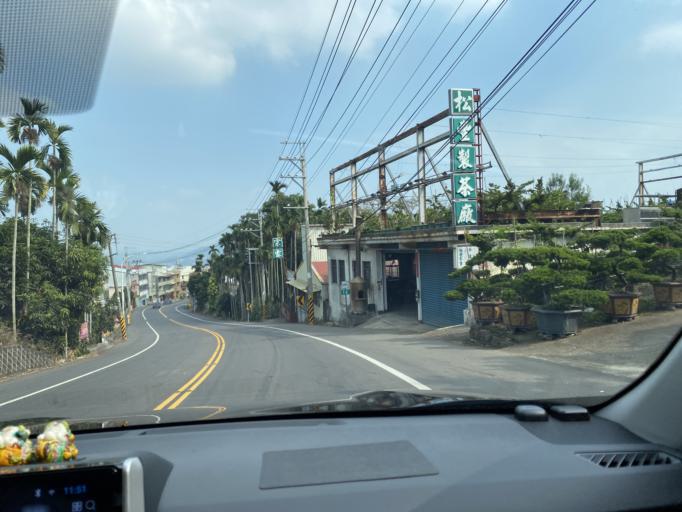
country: TW
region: Taiwan
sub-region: Nantou
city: Nantou
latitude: 23.8335
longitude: 120.6567
